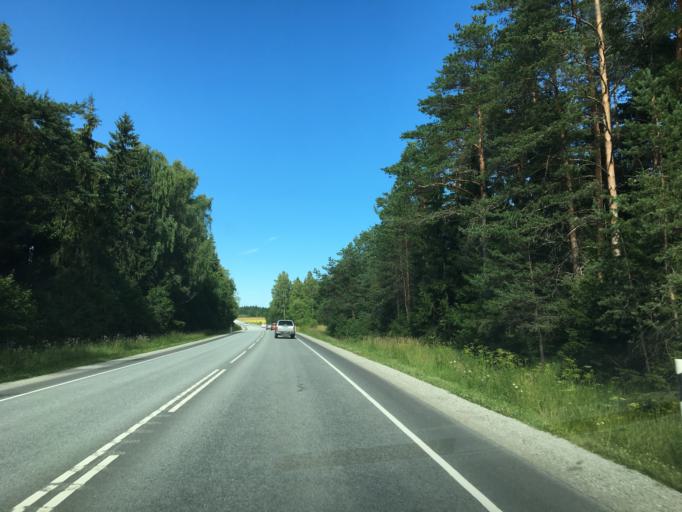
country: EE
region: Harju
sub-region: Keila linn
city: Keila
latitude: 59.2090
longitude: 24.4282
